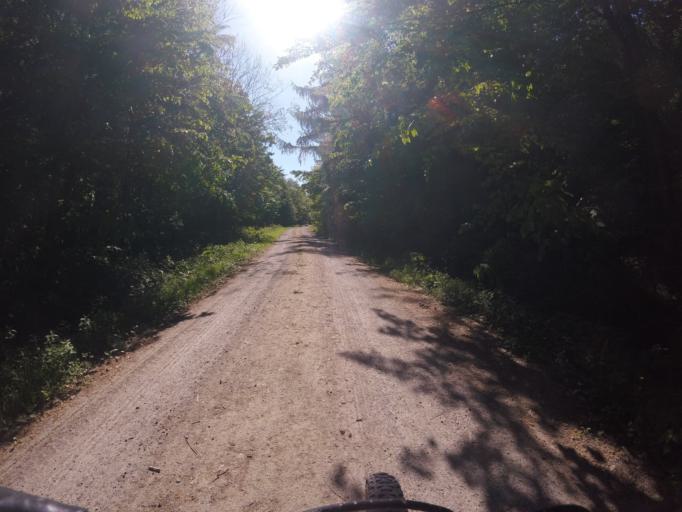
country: DE
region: Baden-Wuerttemberg
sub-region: Regierungsbezirk Stuttgart
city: Spiegelberg
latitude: 49.0069
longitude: 9.4194
